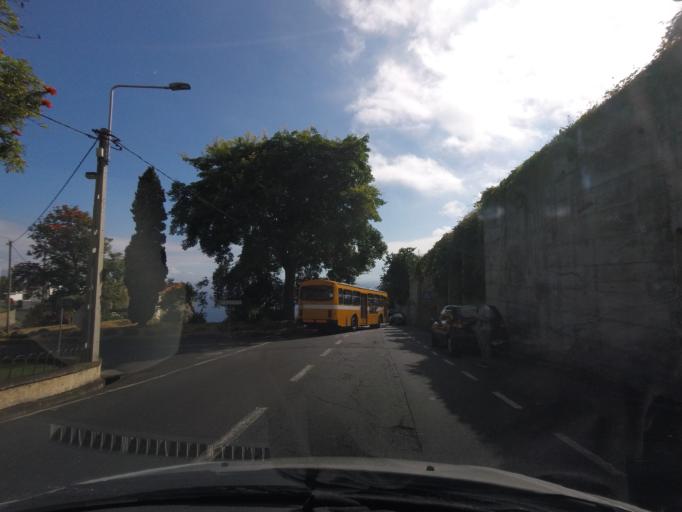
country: PT
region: Madeira
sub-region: Funchal
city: Nossa Senhora do Monte
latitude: 32.6582
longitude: -16.8907
